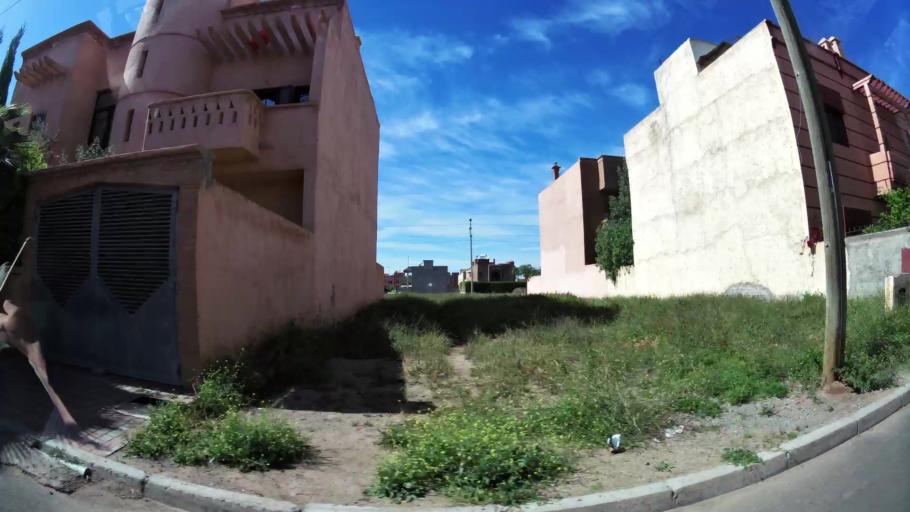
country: MA
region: Marrakech-Tensift-Al Haouz
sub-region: Marrakech
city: Marrakesh
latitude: 31.6413
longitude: -8.0442
